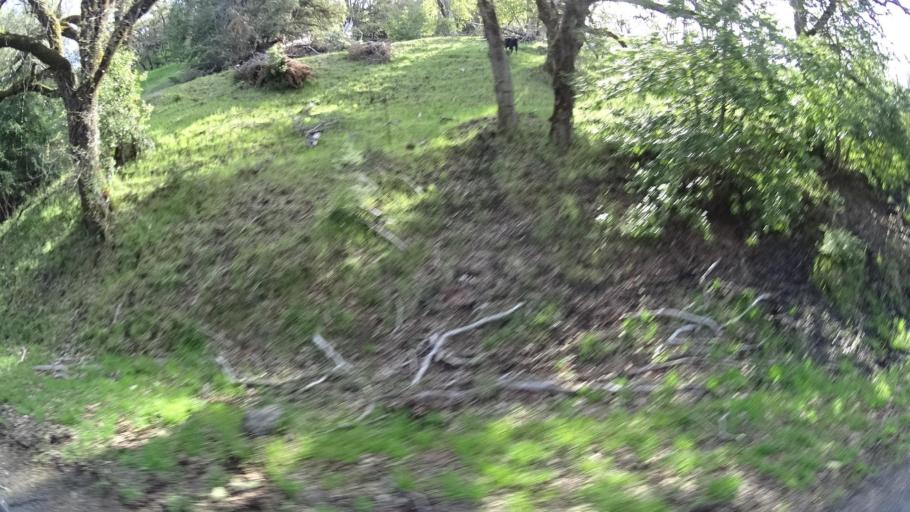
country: US
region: California
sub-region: Humboldt County
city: Hydesville
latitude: 40.6421
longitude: -123.9050
